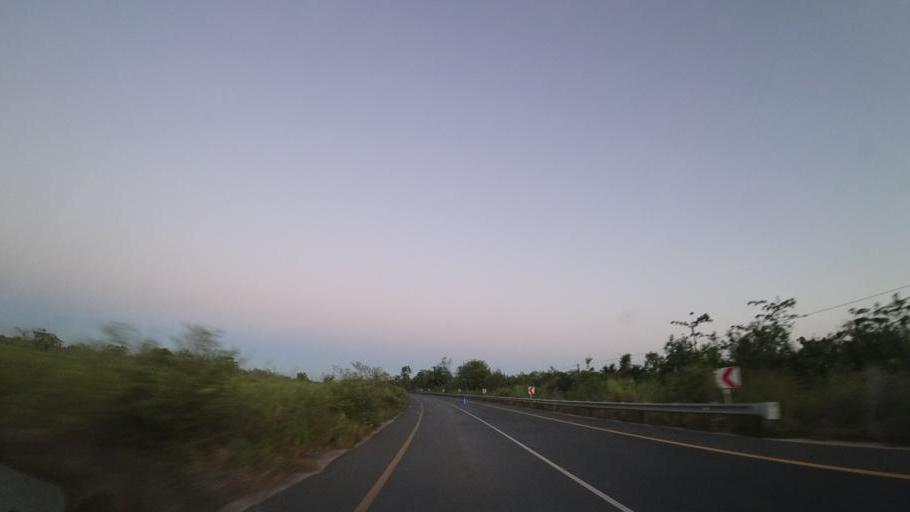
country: MZ
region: Sofala
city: Dondo
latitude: -19.5541
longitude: 34.6523
